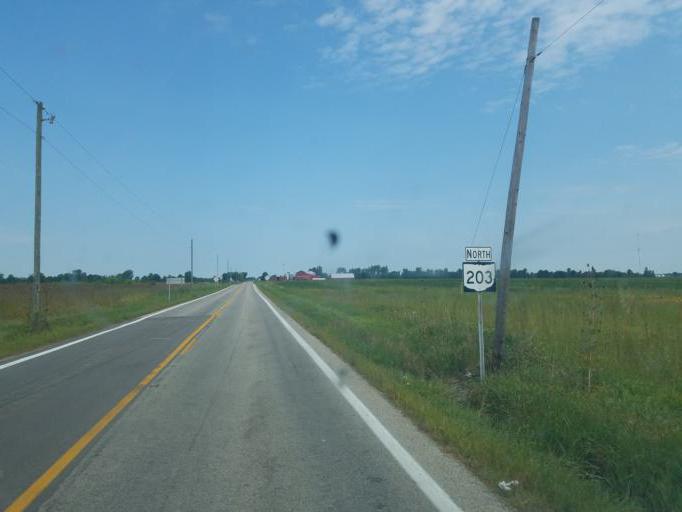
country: US
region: Ohio
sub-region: Marion County
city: Marion
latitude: 40.5865
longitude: -83.2174
